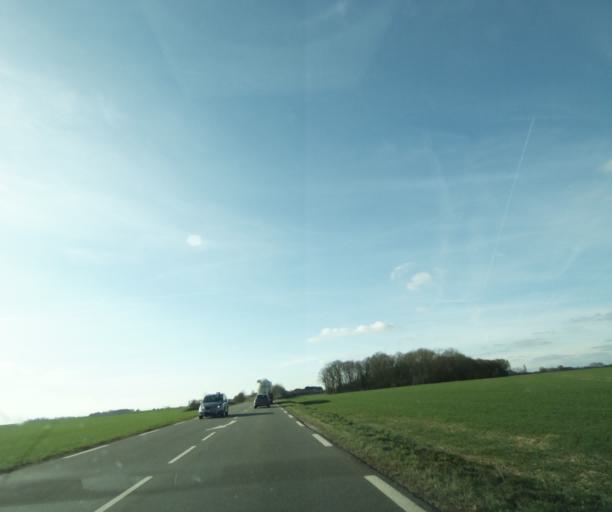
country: FR
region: Ile-de-France
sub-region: Departement des Yvelines
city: Ablis
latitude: 48.4722
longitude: 1.8624
